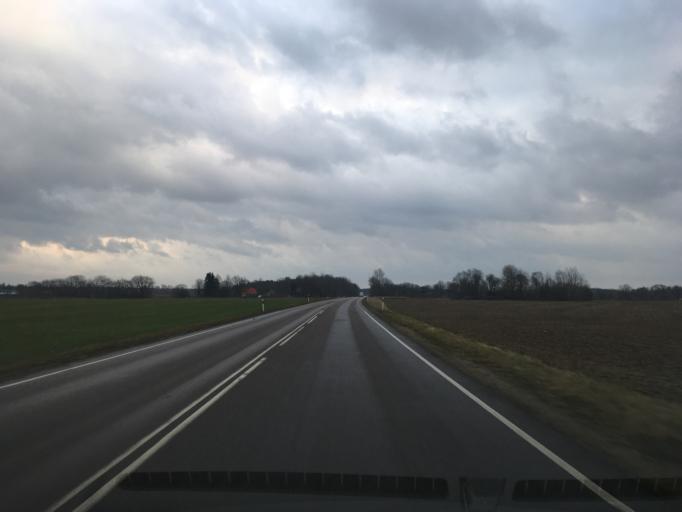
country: EE
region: Harju
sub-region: Anija vald
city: Kehra
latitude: 59.3289
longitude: 25.3219
